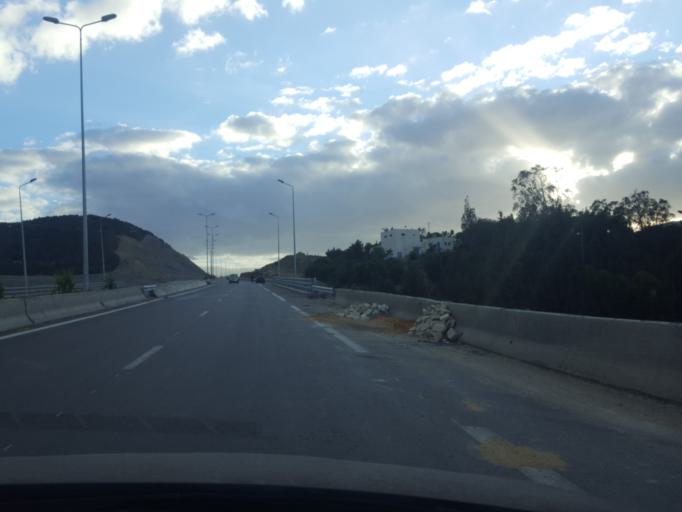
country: TN
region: Tunis
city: Hammam-Lif
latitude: 36.6971
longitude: 10.3993
